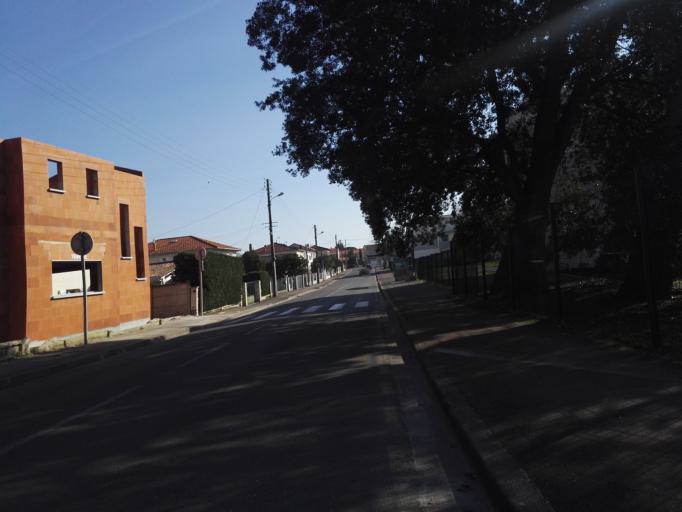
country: FR
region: Aquitaine
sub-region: Departement de la Gironde
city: Talence
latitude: 44.7989
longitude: -0.5872
